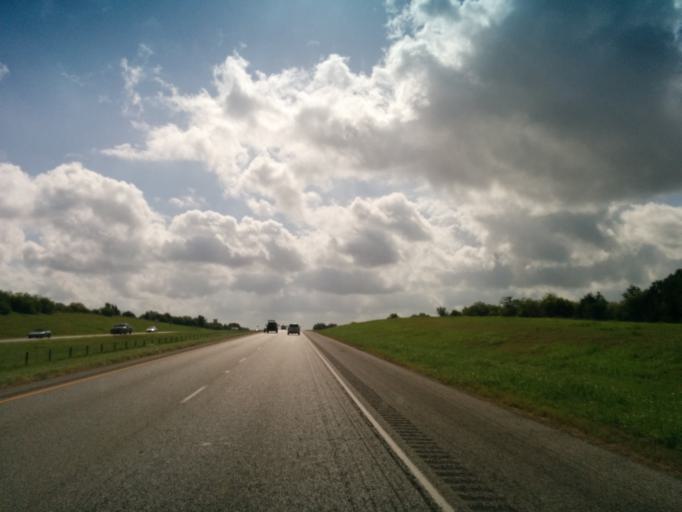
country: US
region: Texas
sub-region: Gonzales County
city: Waelder
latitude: 29.6642
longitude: -97.3622
